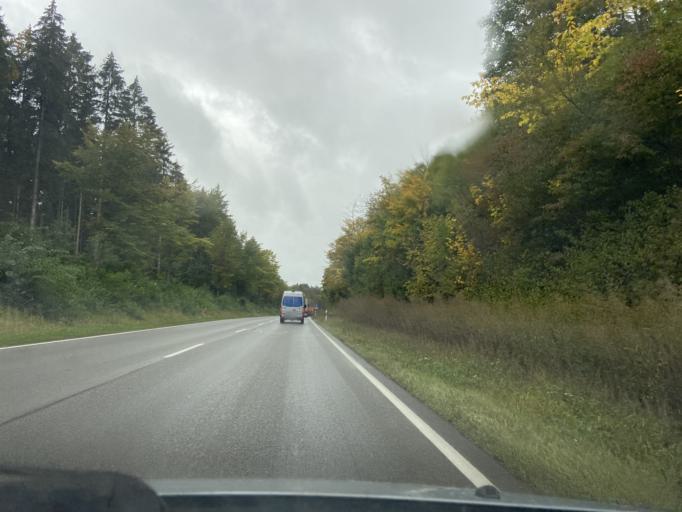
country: DE
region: Baden-Wuerttemberg
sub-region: Tuebingen Region
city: Messkirch
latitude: 47.9845
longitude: 9.0561
